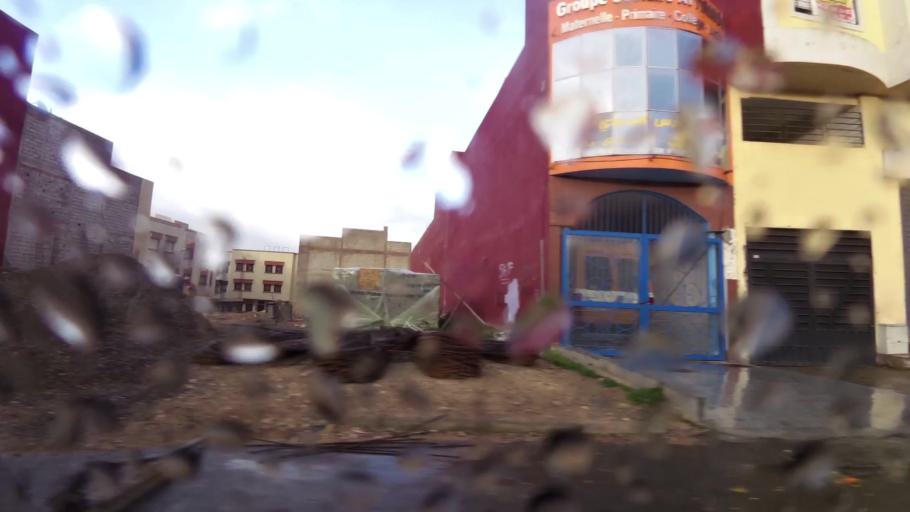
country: MA
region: Doukkala-Abda
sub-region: El-Jadida
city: El Jadida
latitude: 33.2264
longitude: -8.4965
